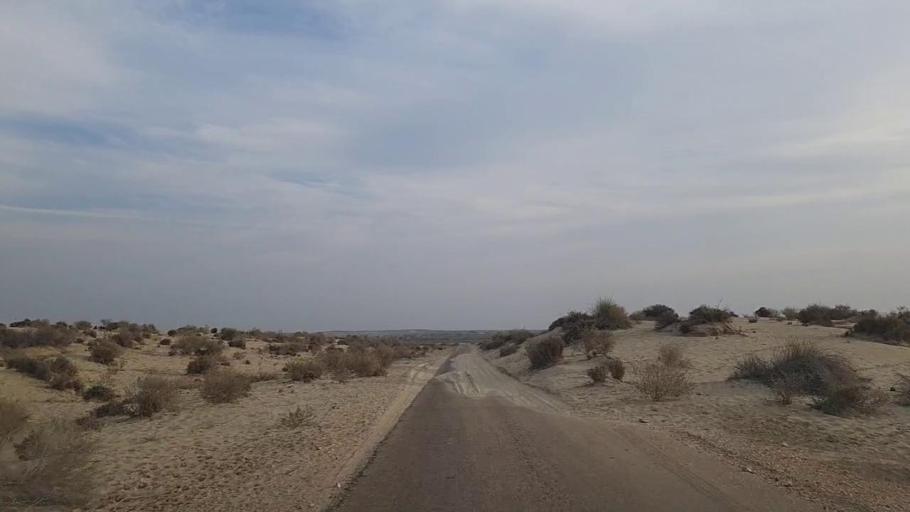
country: PK
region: Sindh
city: Daur
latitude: 26.5007
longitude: 68.5206
